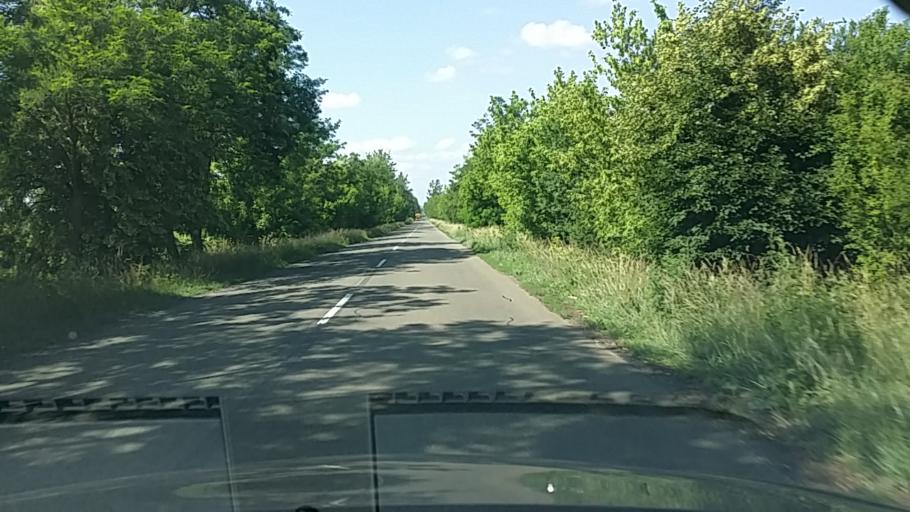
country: HU
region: Komarom-Esztergom
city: Esztergom
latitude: 47.8937
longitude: 18.7756
